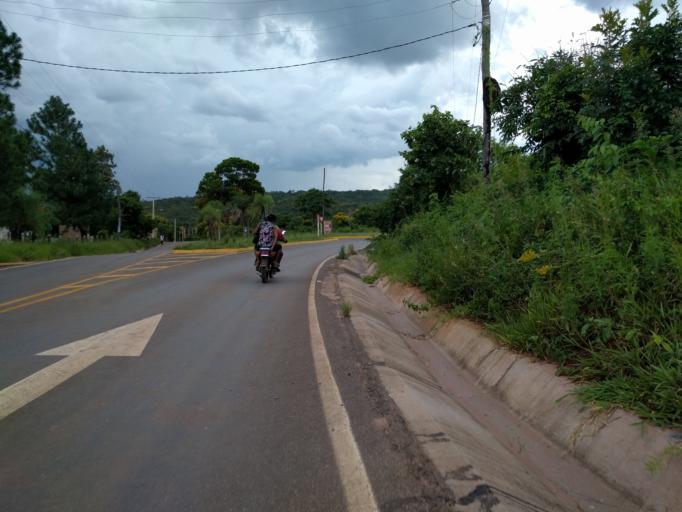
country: BO
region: Santa Cruz
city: Robore
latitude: -18.3421
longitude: -59.6016
